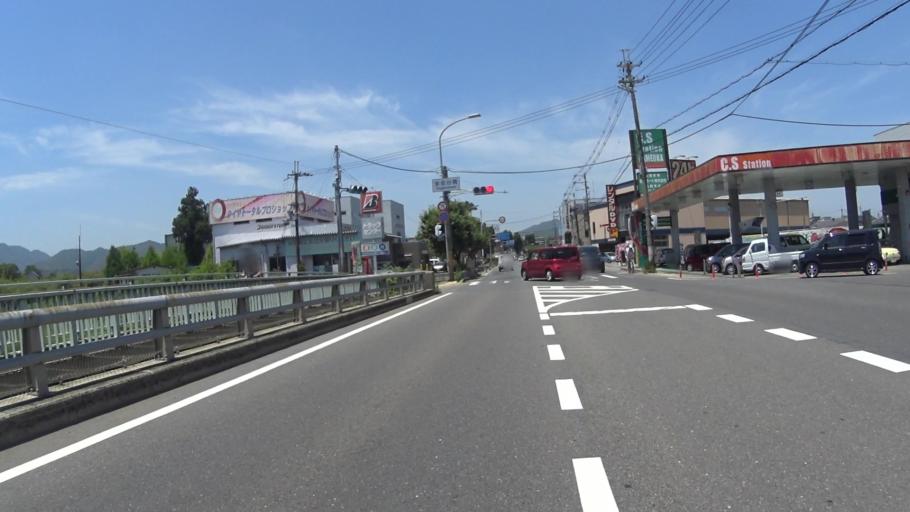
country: JP
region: Kyoto
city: Ayabe
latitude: 35.2314
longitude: 135.2233
